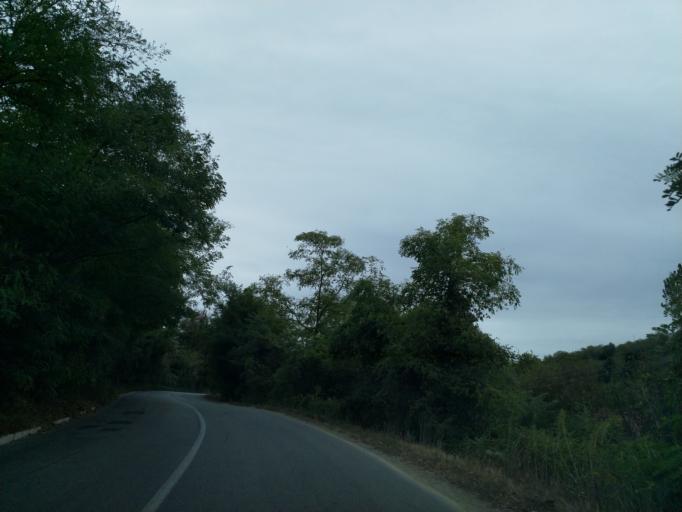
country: RS
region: Central Serbia
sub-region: Pomoravski Okrug
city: Jagodina
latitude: 44.0487
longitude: 21.1826
